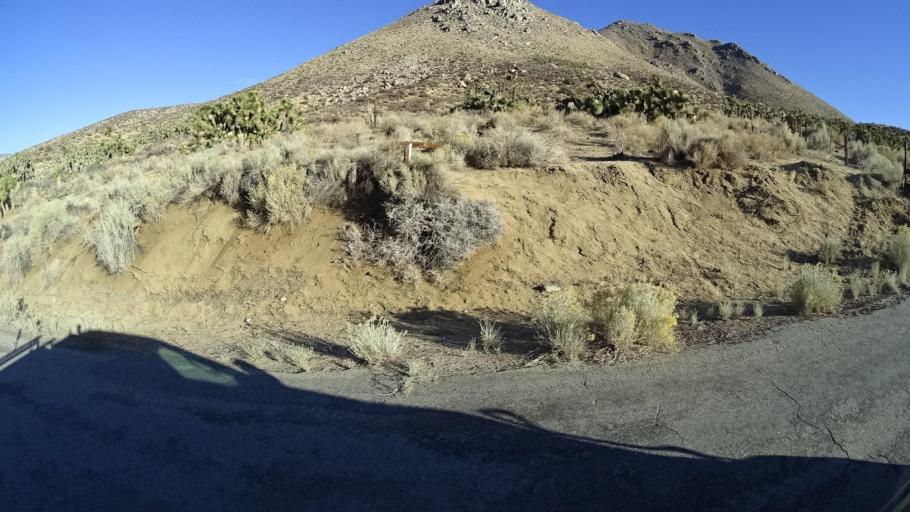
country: US
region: California
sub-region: Kern County
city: Weldon
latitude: 35.4718
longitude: -118.2112
